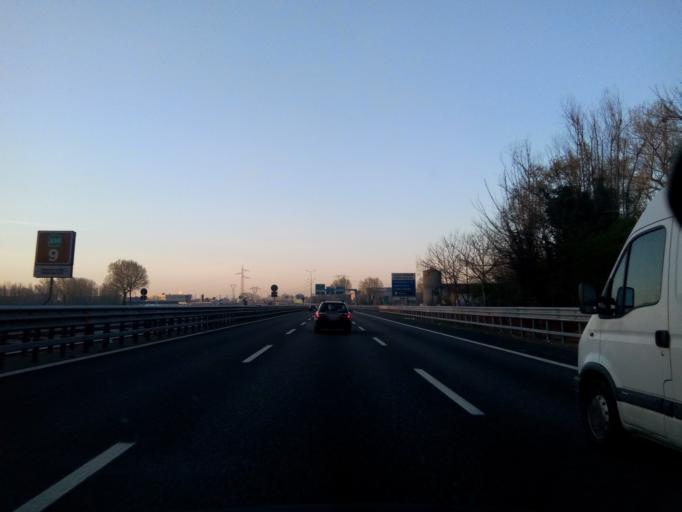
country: IT
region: Lombardy
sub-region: Citta metropolitana di Milano
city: Trezzano sul Naviglio
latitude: 45.4353
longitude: 9.0742
